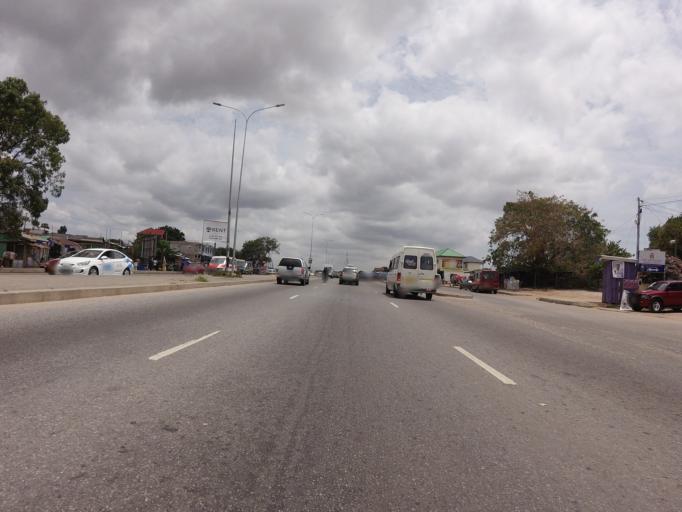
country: GH
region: Greater Accra
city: Gbawe
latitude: 5.5796
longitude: -0.2654
